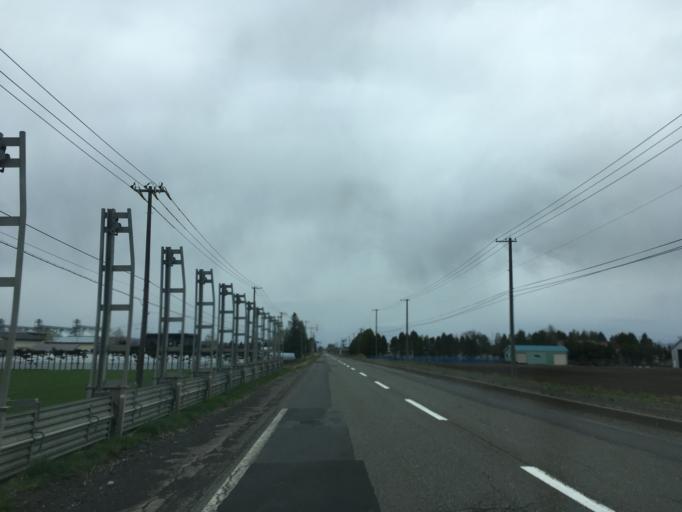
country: JP
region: Hokkaido
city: Chitose
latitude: 42.9299
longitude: 141.8071
